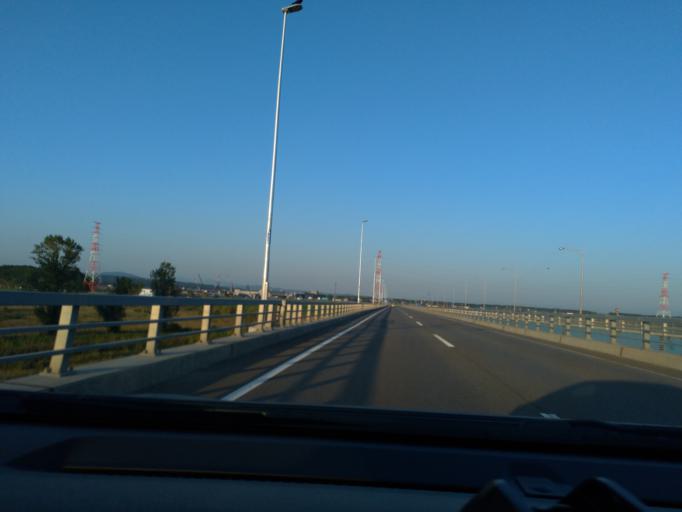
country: JP
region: Hokkaido
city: Ishikari
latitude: 43.1741
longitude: 141.4222
